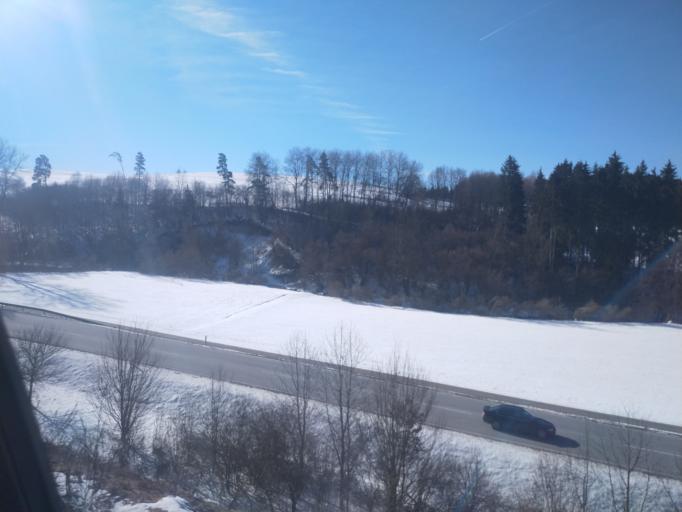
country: DE
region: Baden-Wuerttemberg
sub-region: Freiburg Region
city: Aldingen
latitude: 48.1182
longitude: 8.6852
